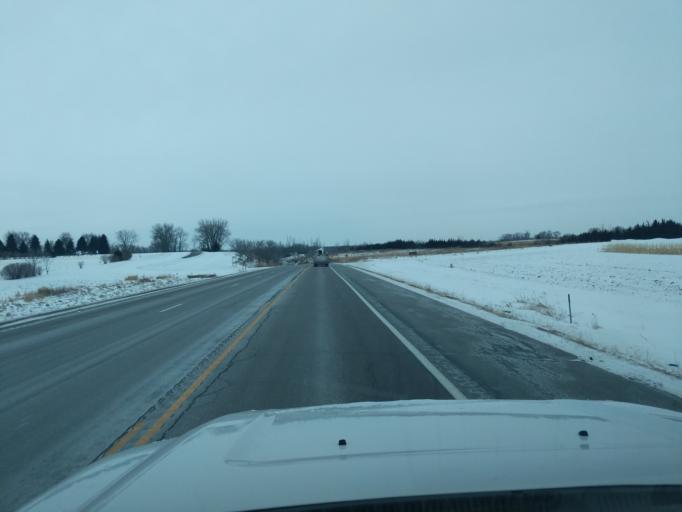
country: US
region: Minnesota
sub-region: Redwood County
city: Redwood Falls
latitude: 44.5631
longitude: -94.9977
